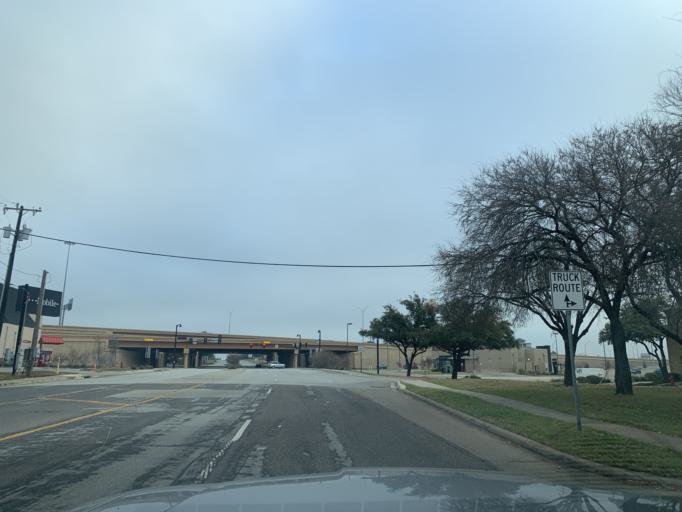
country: US
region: Texas
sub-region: Tarrant County
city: Bedford
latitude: 32.8379
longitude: -97.1522
